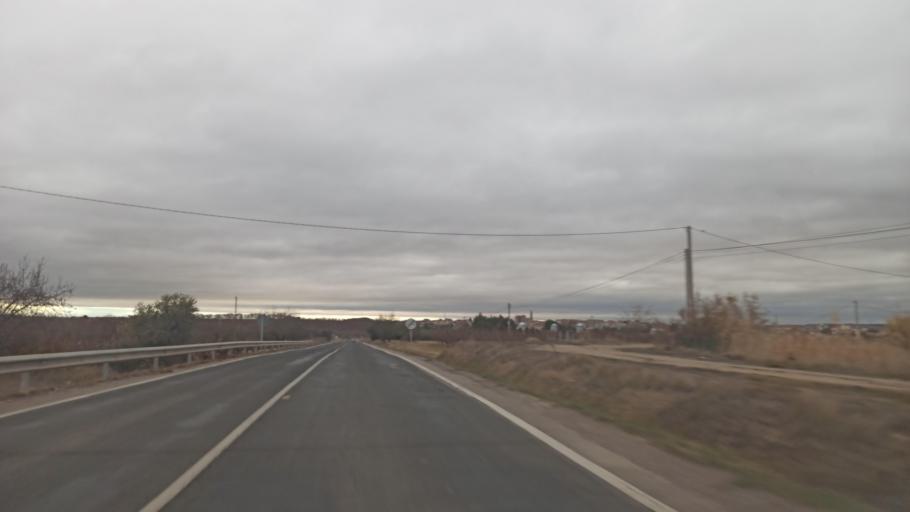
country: ES
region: Catalonia
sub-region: Provincia de Lleida
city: Juneda
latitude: 41.5128
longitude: 0.8476
